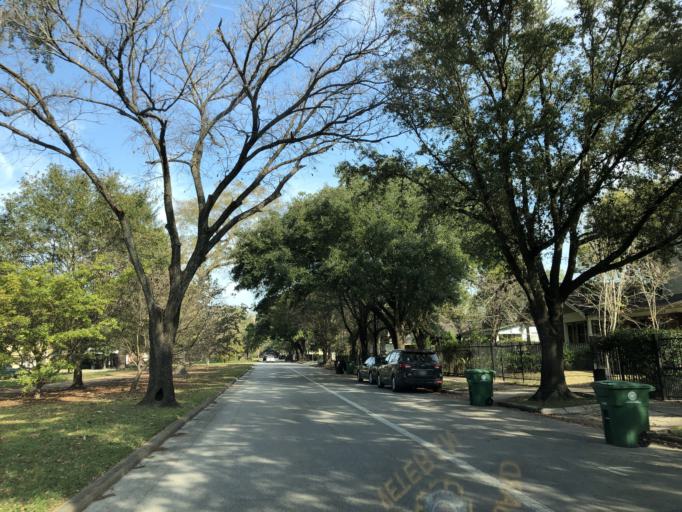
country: US
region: Texas
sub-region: Harris County
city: Houston
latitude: 29.7933
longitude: -95.3976
